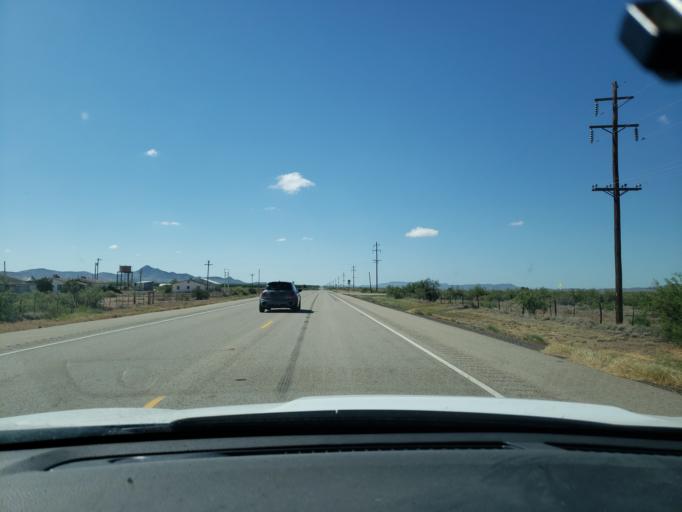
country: US
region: Texas
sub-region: Culberson County
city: Van Horn
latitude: 30.8733
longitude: -104.7836
